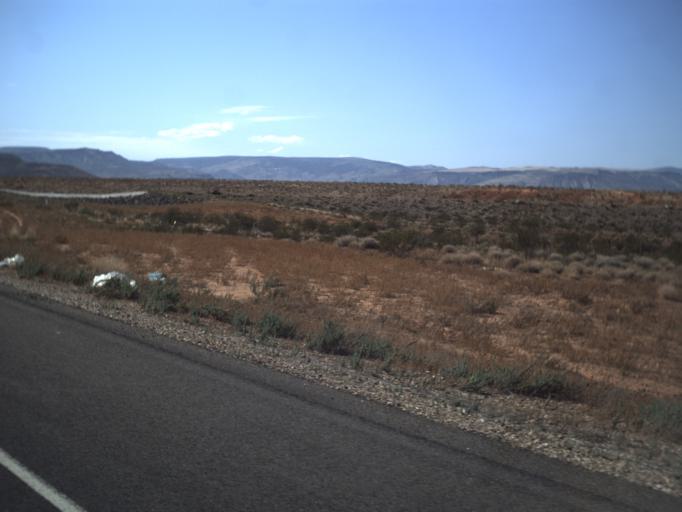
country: US
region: Utah
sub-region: Washington County
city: Washington
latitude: 37.0534
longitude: -113.4859
